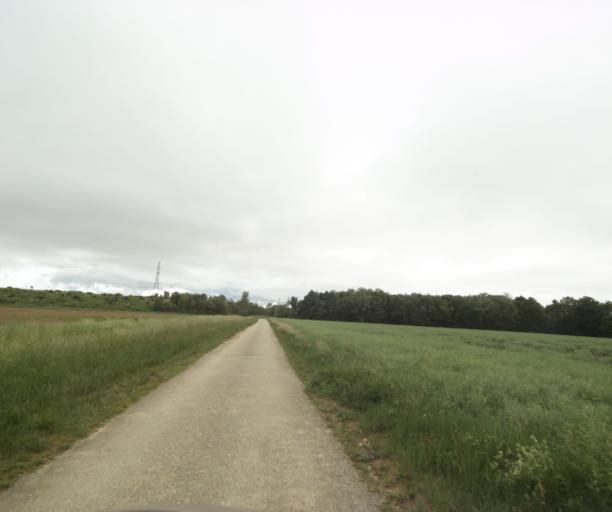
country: FR
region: Rhone-Alpes
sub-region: Departement de l'Ain
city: Tramoyes
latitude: 45.8613
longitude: 4.9539
